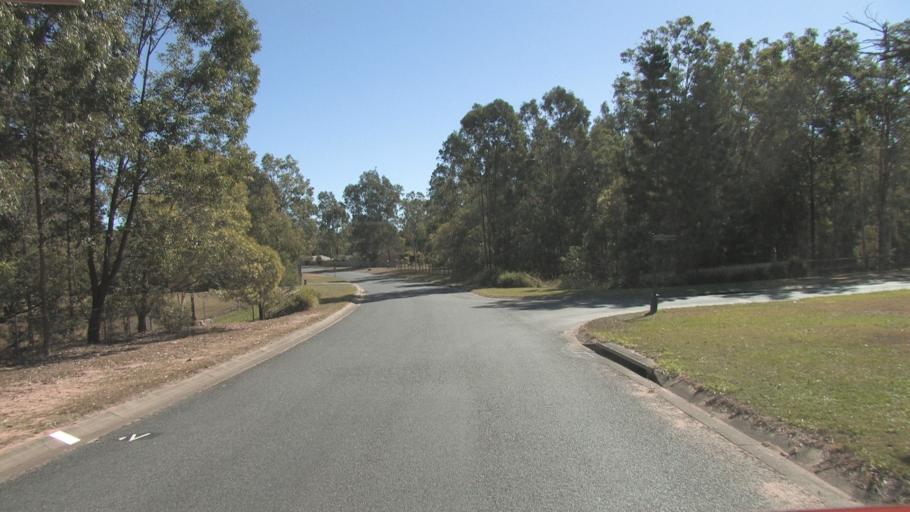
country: AU
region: Queensland
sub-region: Logan
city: North Maclean
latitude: -27.8203
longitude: 152.9533
